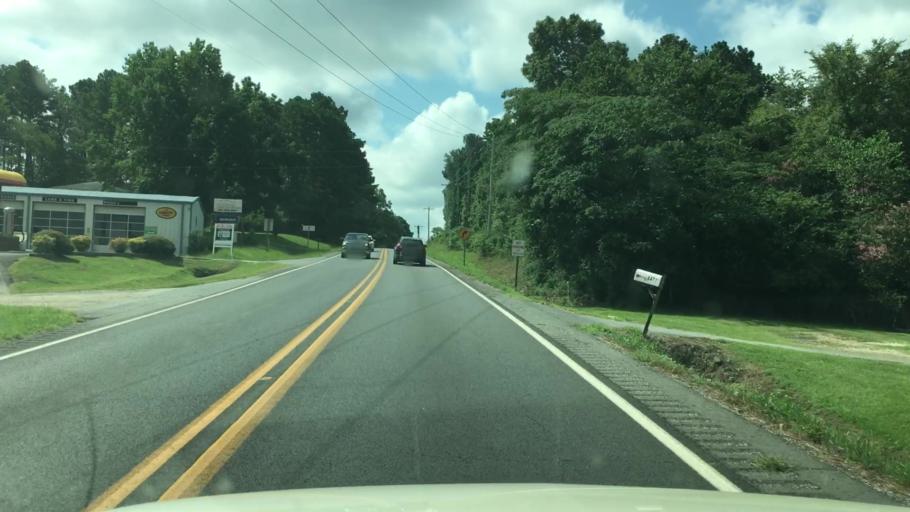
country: US
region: Arkansas
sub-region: Garland County
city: Lake Hamilton
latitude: 34.3129
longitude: -93.1696
